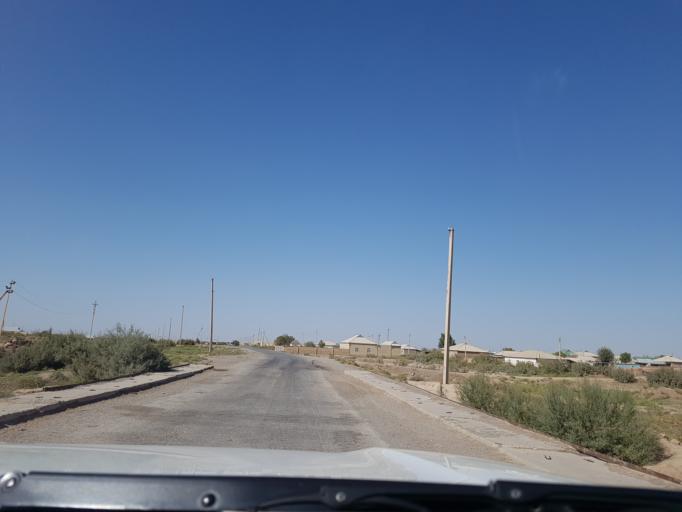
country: IR
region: Razavi Khorasan
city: Sarakhs
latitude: 36.5136
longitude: 61.2530
